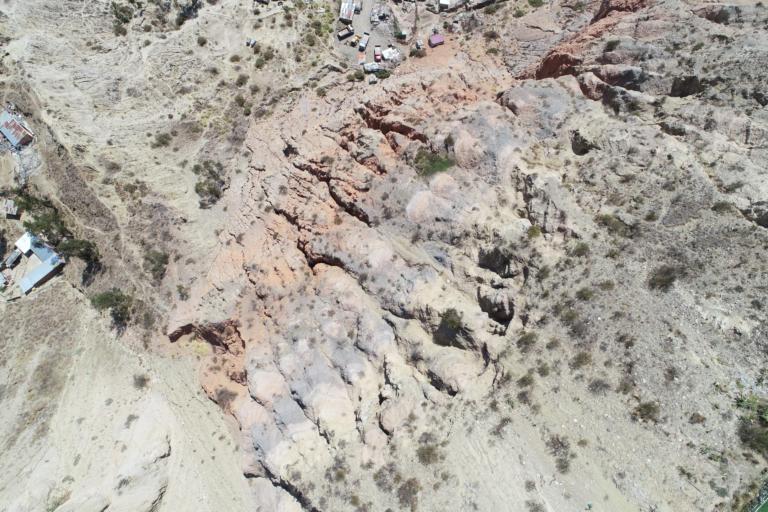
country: BO
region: La Paz
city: La Paz
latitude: -16.5283
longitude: -68.0917
